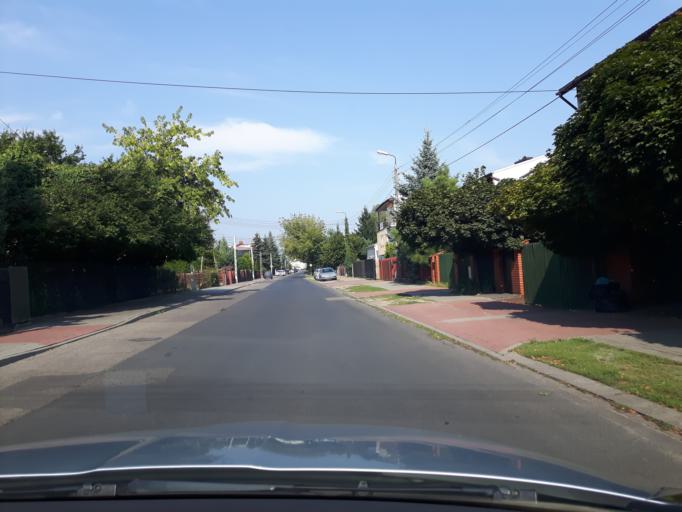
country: PL
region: Masovian Voivodeship
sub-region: Warszawa
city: Targowek
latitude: 52.2778
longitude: 21.0726
